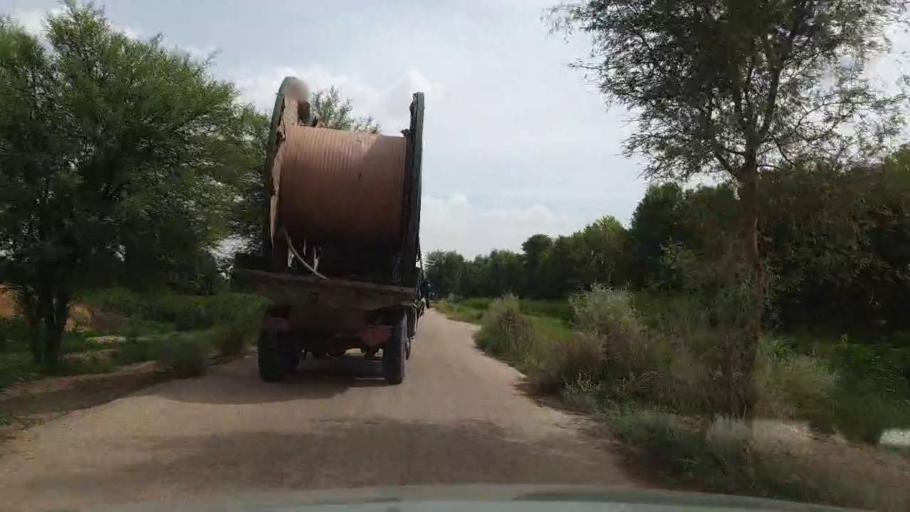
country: PK
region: Sindh
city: Kot Diji
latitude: 27.1565
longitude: 69.0352
